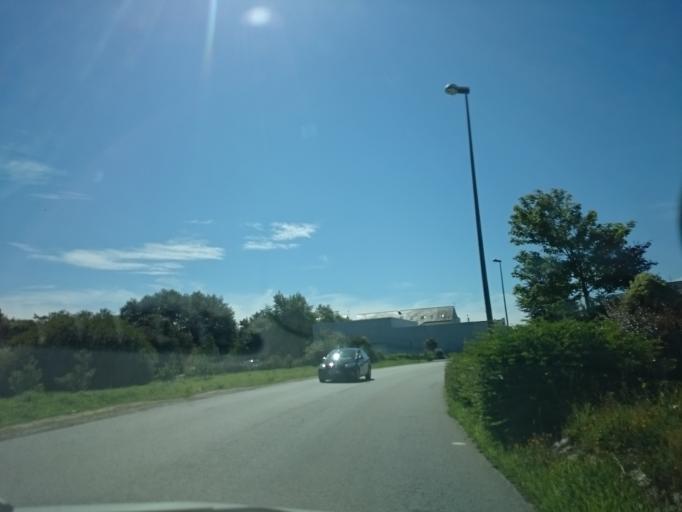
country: FR
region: Brittany
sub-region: Departement du Finistere
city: Saint-Renan
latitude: 48.4361
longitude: -4.6224
